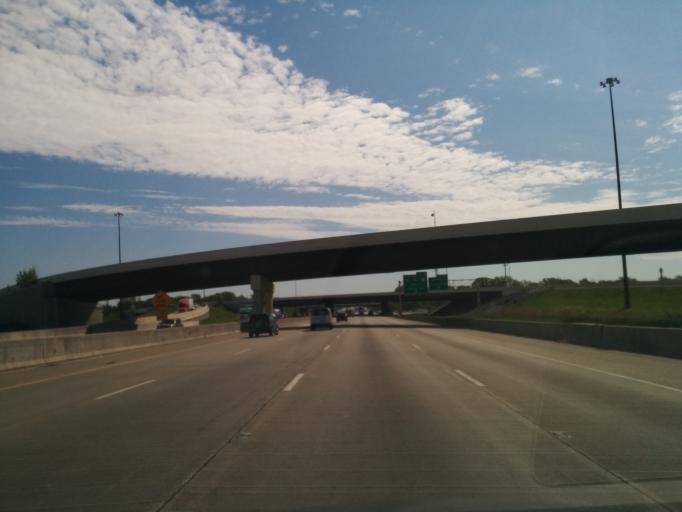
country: US
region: Indiana
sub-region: Lake County
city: New Chicago
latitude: 41.5684
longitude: -87.3039
